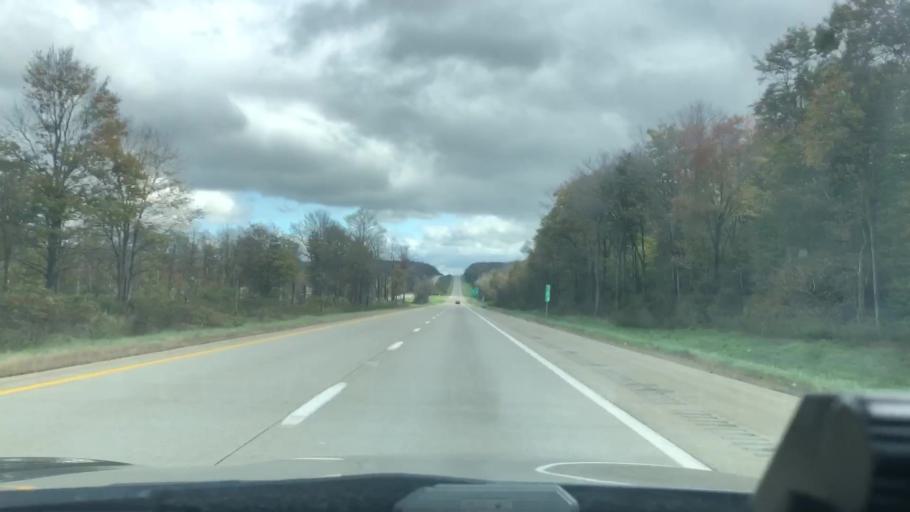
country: US
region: Pennsylvania
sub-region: Monroe County
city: Pocono Pines
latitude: 41.2091
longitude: -75.4673
